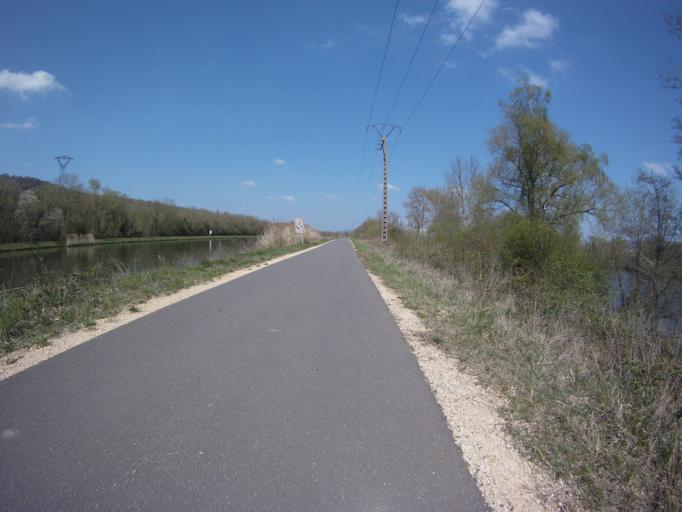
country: FR
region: Lorraine
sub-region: Departement de Meurthe-et-Moselle
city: Dieulouard
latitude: 48.8526
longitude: 6.0775
